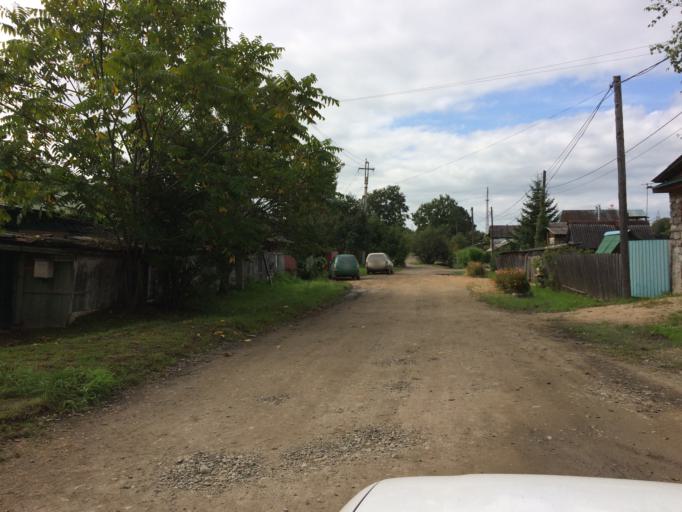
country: RU
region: Primorskiy
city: Dal'nerechensk
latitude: 45.9188
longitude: 133.7125
